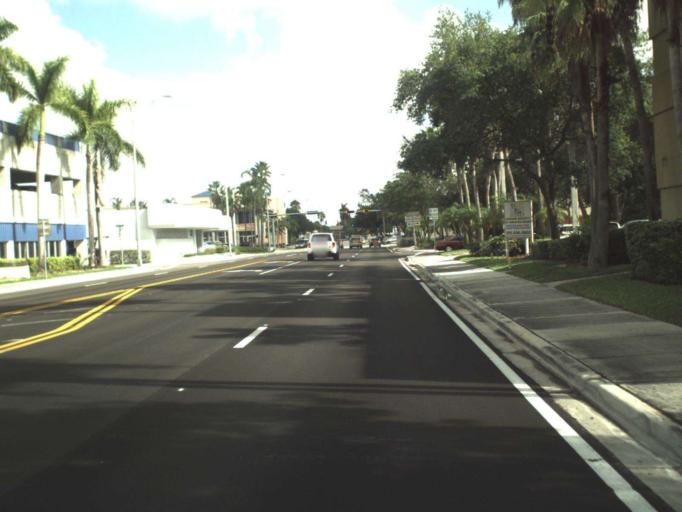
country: US
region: Florida
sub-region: Miami-Dade County
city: North Miami Beach
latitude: 25.9245
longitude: -80.1558
